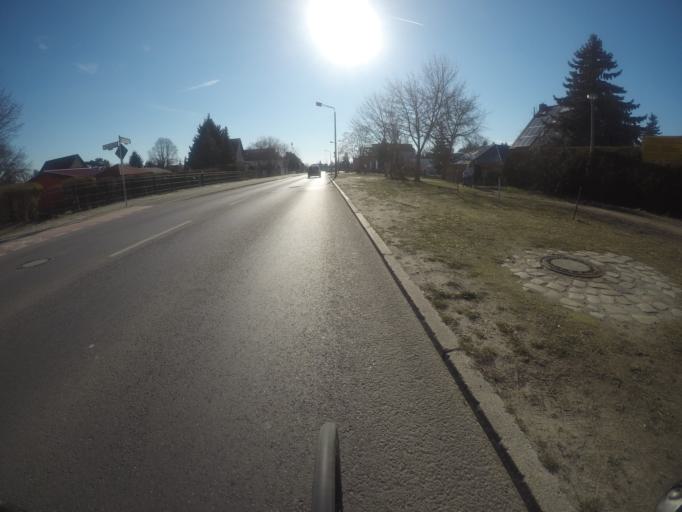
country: DE
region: Berlin
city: Kaulsdorf
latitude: 52.4976
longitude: 13.5778
